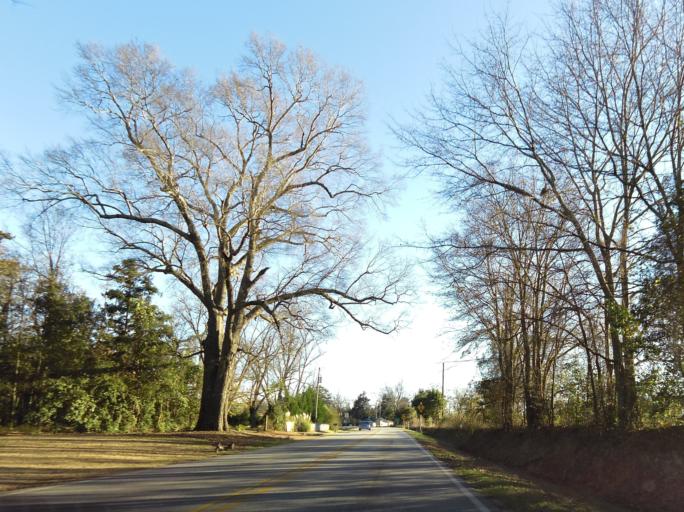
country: US
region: Georgia
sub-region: Houston County
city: Centerville
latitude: 32.6615
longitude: -83.6994
